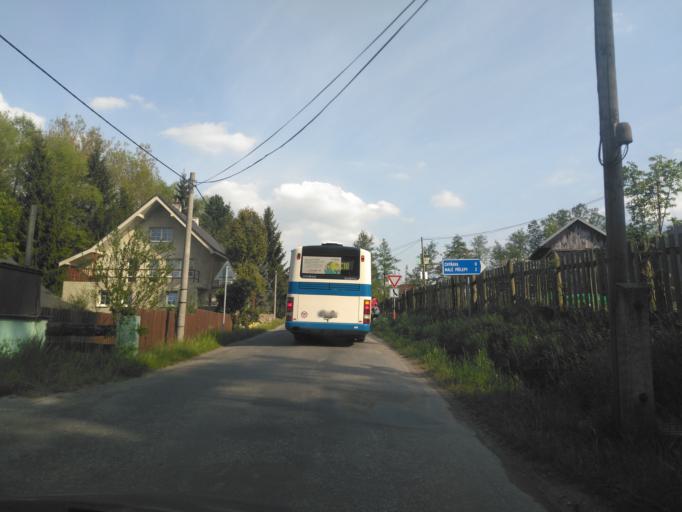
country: CZ
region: Central Bohemia
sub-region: Okres Beroun
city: Lodenice
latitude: 50.0114
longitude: 14.1476
